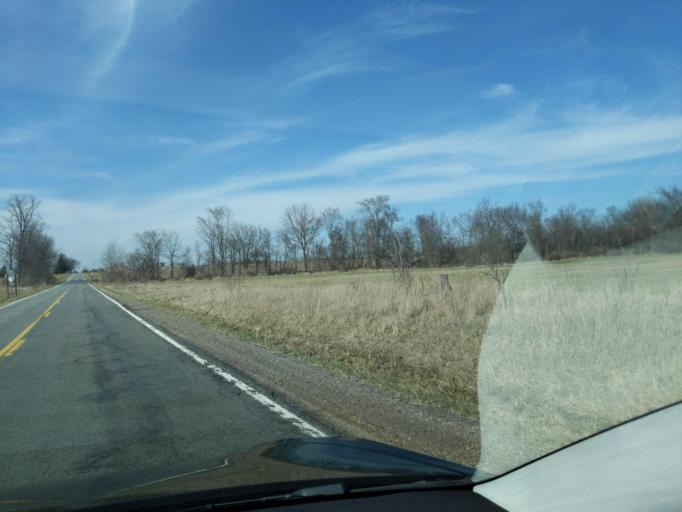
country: US
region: Michigan
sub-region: Ingham County
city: Williamston
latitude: 42.6452
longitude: -84.3107
